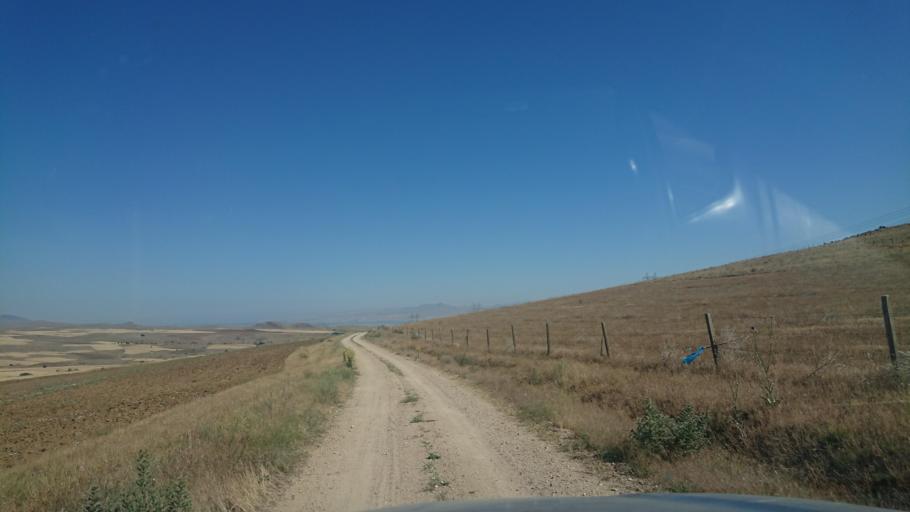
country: TR
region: Aksaray
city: Agacoren
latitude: 38.9157
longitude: 33.8935
